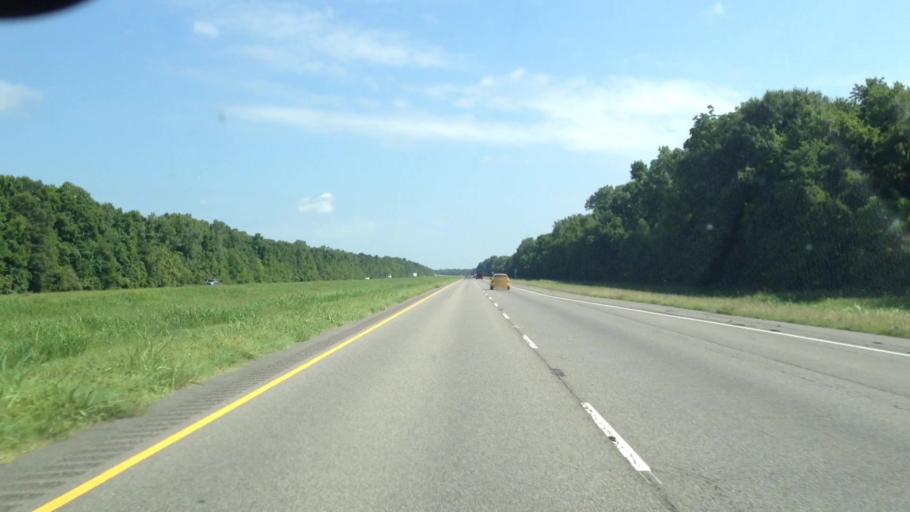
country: US
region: Louisiana
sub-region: Avoyelles Parish
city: Bunkie
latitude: 30.8723
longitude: -92.2274
